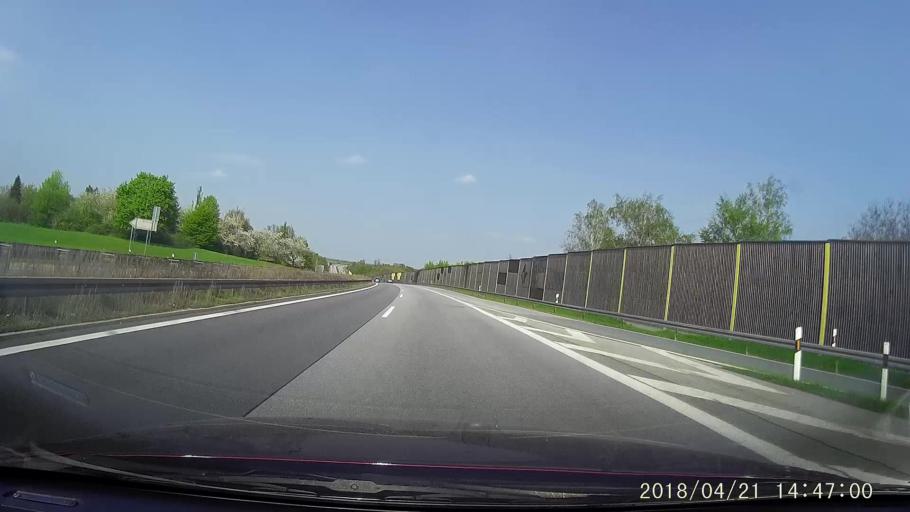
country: DE
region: Saxony
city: Bautzen
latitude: 51.1888
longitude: 14.4130
